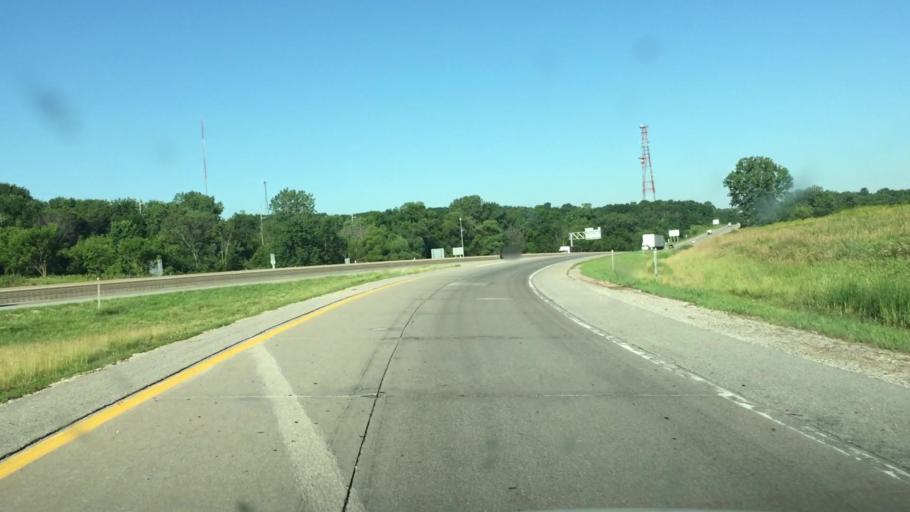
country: US
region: Iowa
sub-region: Johnson County
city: Iowa City
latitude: 41.6872
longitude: -91.5021
